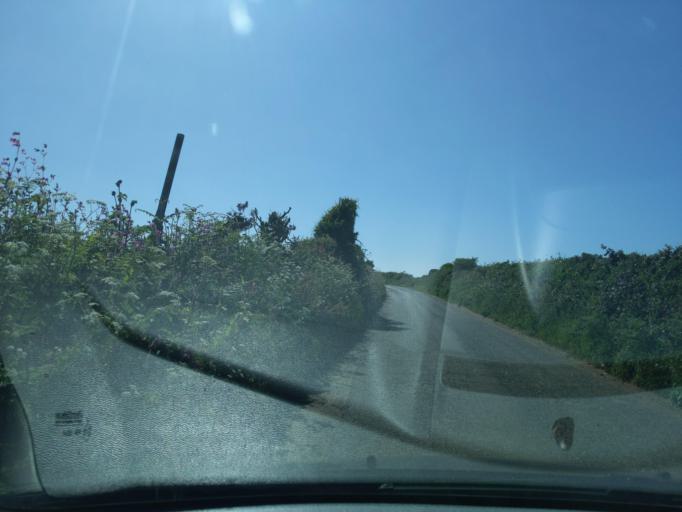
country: GB
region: England
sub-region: Cornwall
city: St. Buryan
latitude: 50.0588
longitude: -5.6137
